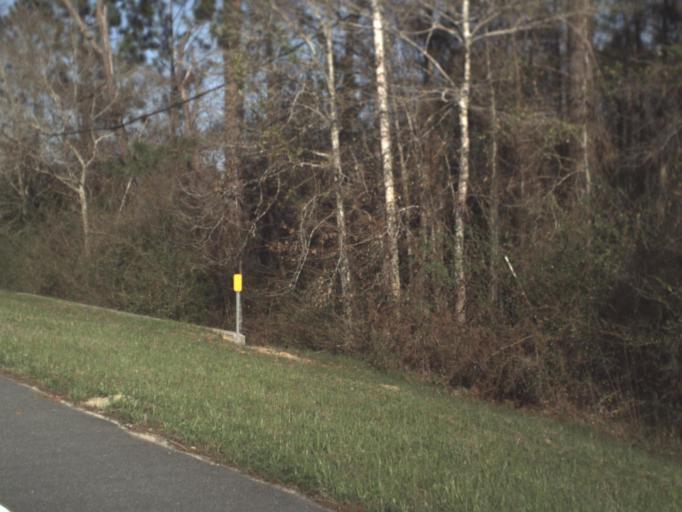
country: US
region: Florida
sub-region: Calhoun County
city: Blountstown
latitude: 30.4084
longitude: -85.2095
